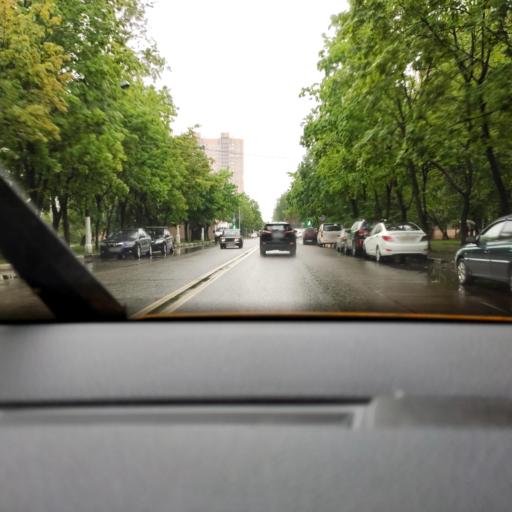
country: RU
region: Moskovskaya
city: Balashikha
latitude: 55.7953
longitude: 37.9696
